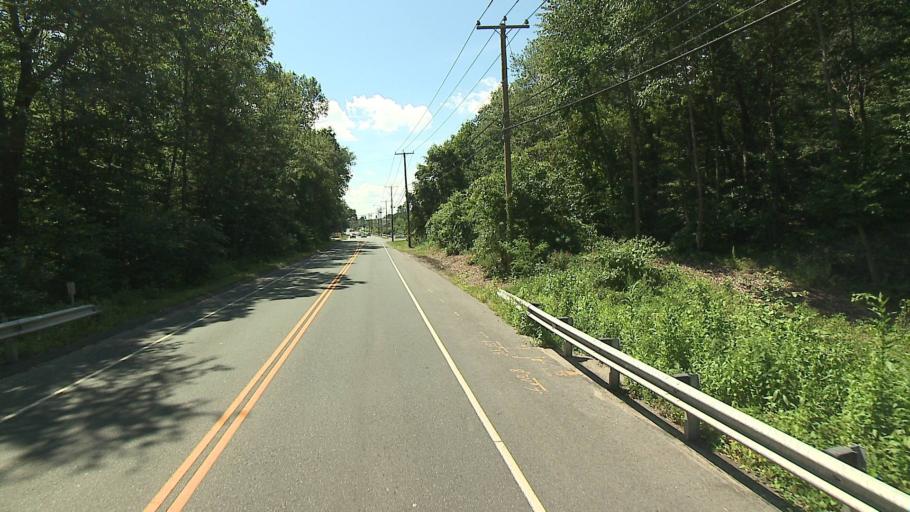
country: US
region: Connecticut
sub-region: Fairfield County
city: Trumbull
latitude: 41.3198
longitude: -73.2132
